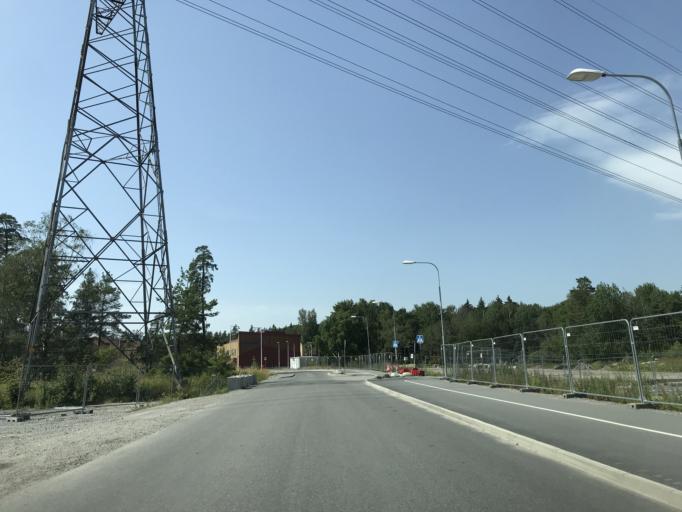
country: SE
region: Stockholm
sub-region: Solna Kommun
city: Rasunda
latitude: 59.3831
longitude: 17.9906
